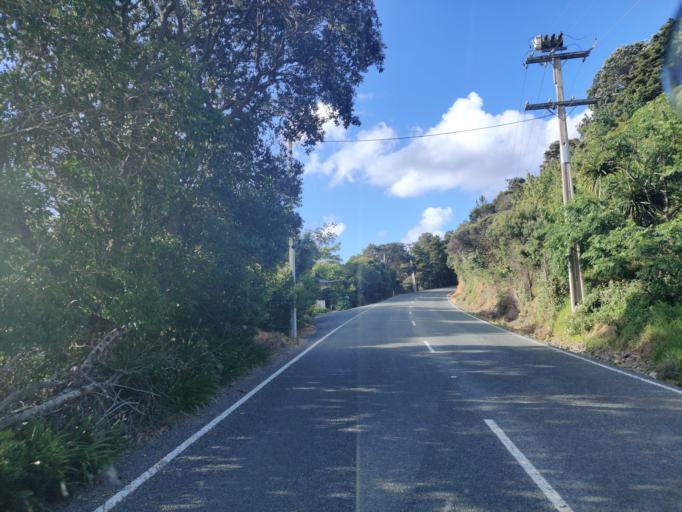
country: NZ
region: Northland
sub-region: Whangarei
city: Ngunguru
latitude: -35.6094
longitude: 174.5236
